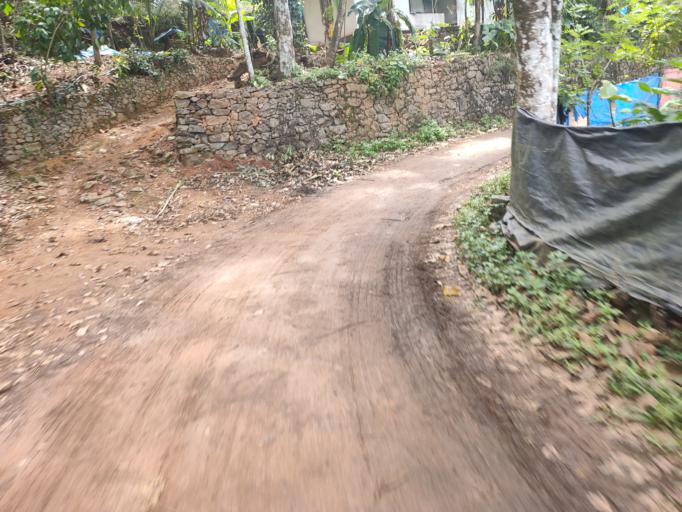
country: IN
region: Kerala
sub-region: Ernakulam
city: Kotamangalam
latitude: 10.0068
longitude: 76.6411
